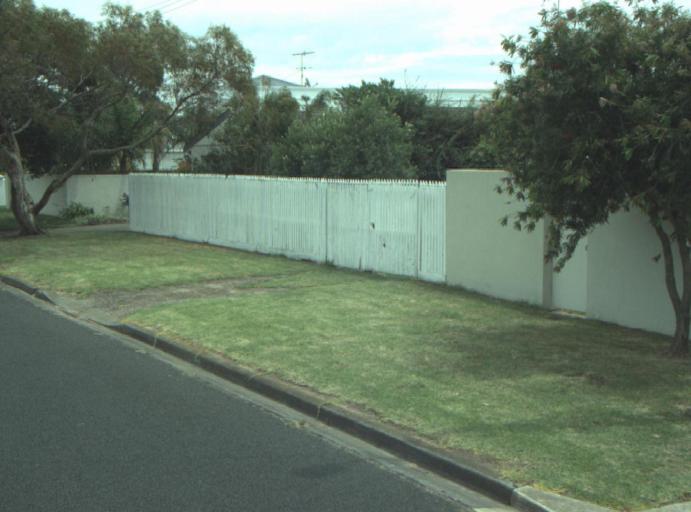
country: AU
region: Victoria
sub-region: Greater Geelong
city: Clifton Springs
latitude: -38.1572
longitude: 144.5539
